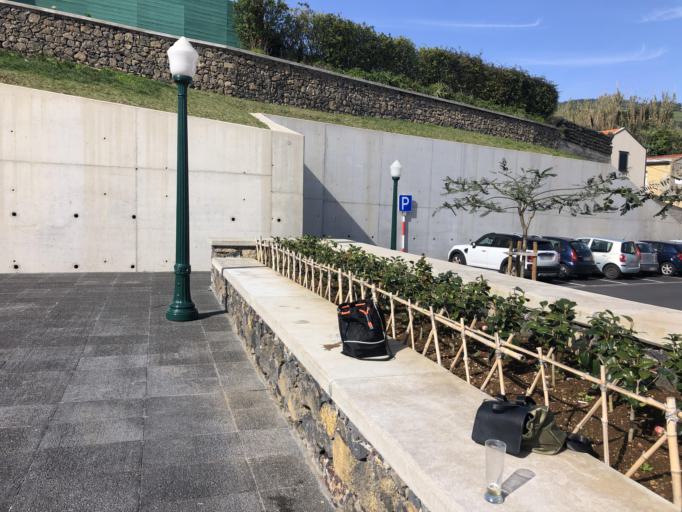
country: PT
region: Azores
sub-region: Vila Franca do Campo
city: Vila Franca do Campo
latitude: 37.7204
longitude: -25.4550
